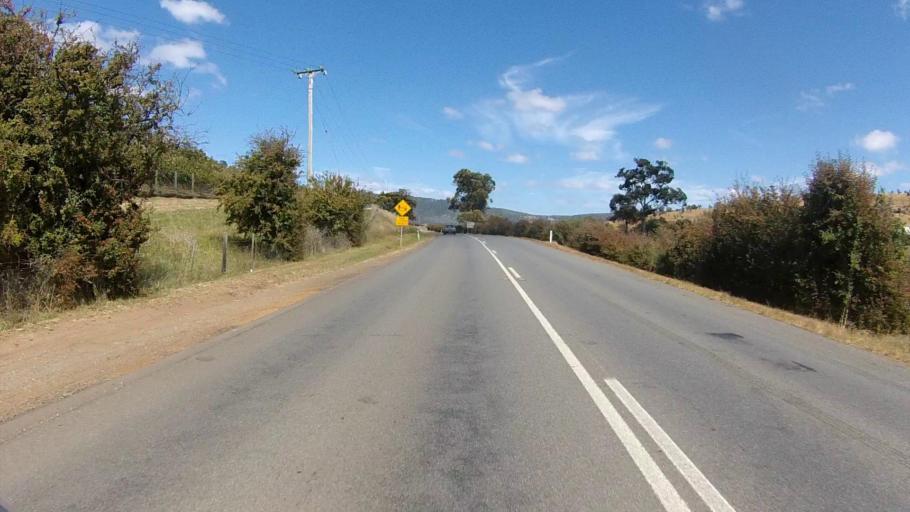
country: AU
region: Tasmania
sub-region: Clarence
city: Cambridge
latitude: -42.7392
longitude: 147.4269
